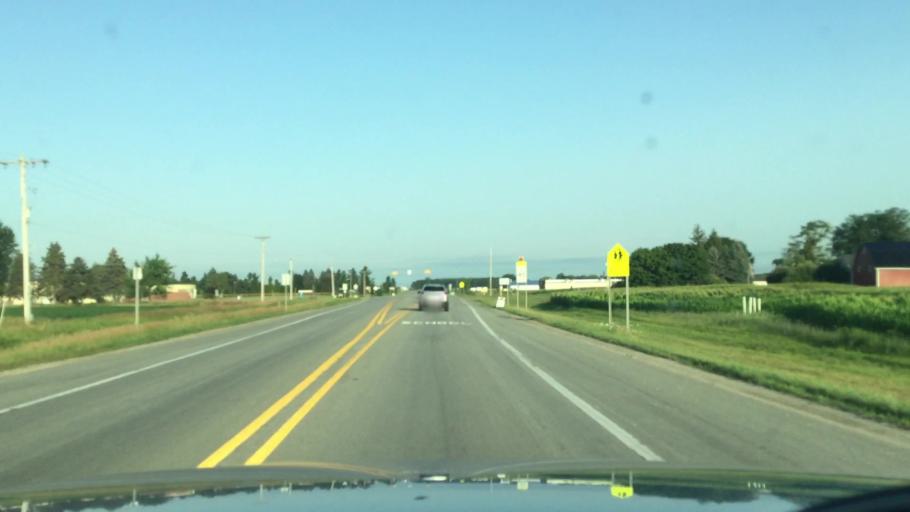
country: US
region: Michigan
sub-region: Montcalm County
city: Carson City
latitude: 43.1763
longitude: -84.7063
